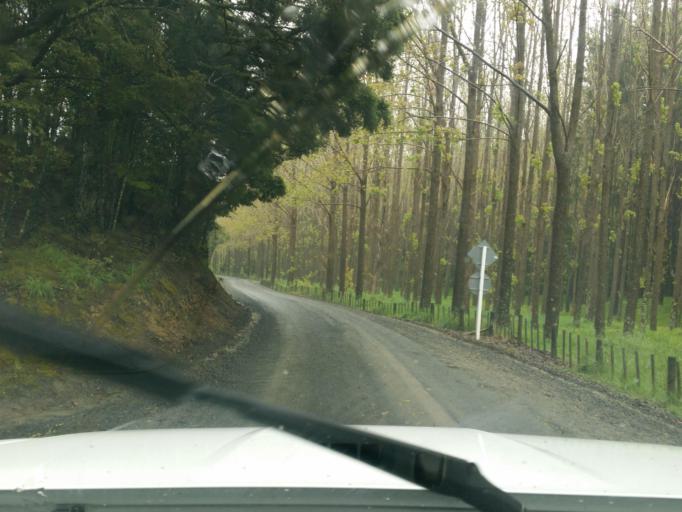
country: NZ
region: Northland
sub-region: Kaipara District
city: Dargaville
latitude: -35.8062
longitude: 173.9969
